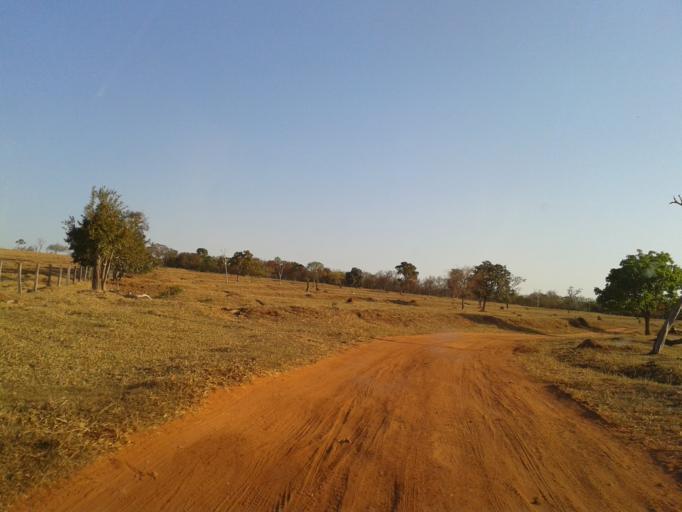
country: BR
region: Minas Gerais
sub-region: Campina Verde
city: Campina Verde
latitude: -19.2587
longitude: -49.6121
